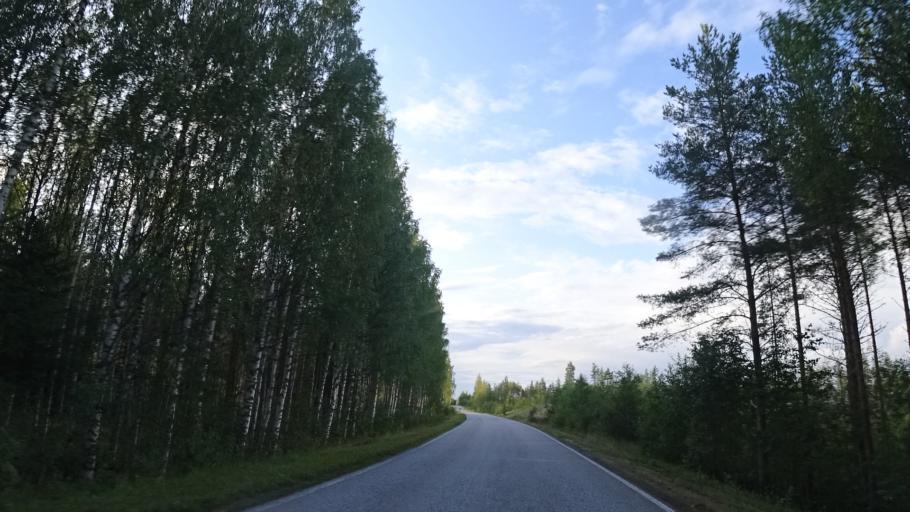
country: FI
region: North Karelia
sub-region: Pielisen Karjala
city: Lieksa
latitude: 63.3504
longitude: 30.2657
